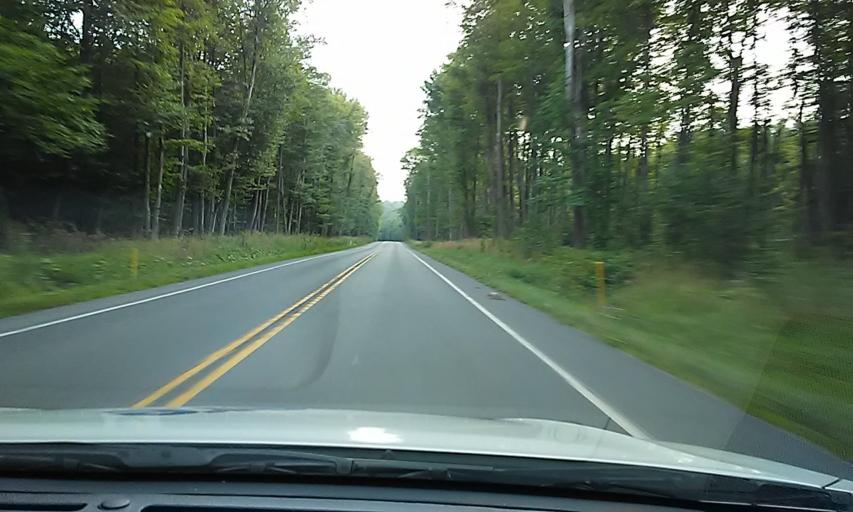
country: US
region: Pennsylvania
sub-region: McKean County
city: Kane
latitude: 41.6138
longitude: -78.8359
